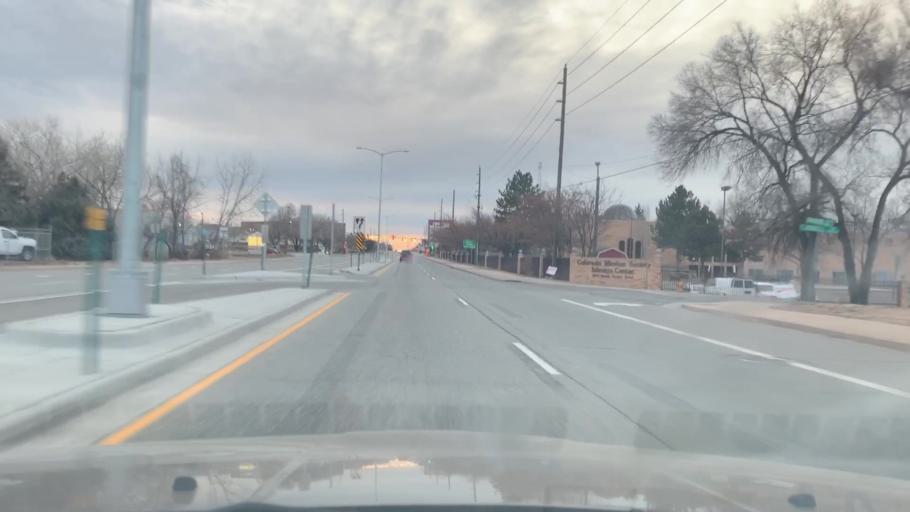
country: US
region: Colorado
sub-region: Arapahoe County
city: Glendale
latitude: 39.6801
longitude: -104.8775
